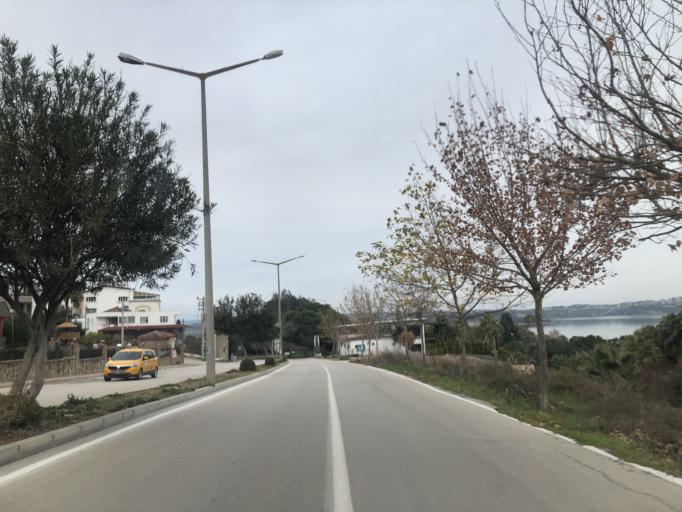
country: TR
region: Adana
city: Adana
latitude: 37.0583
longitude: 35.2987
